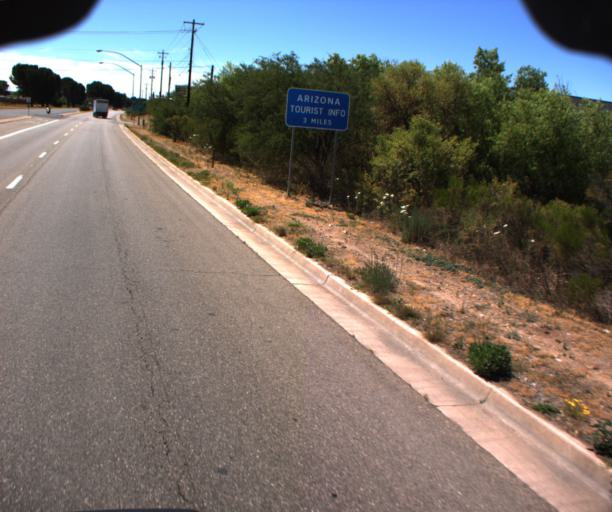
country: US
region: Arizona
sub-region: Santa Cruz County
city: Nogales
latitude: 31.3927
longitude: -110.9552
